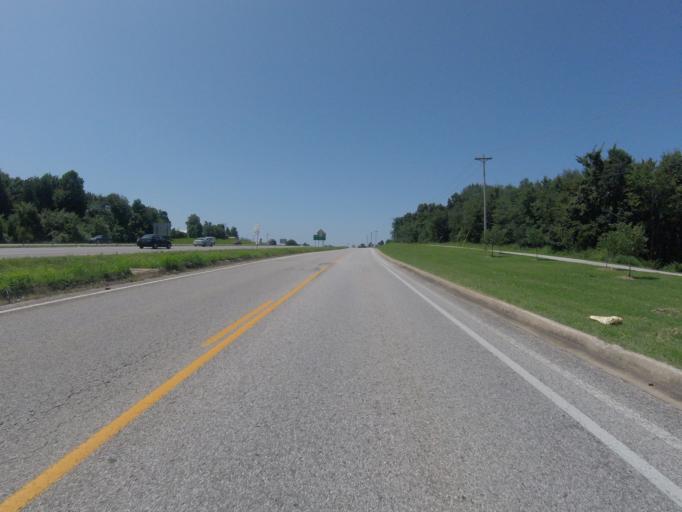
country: US
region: Arkansas
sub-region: Washington County
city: Johnson
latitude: 36.1002
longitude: -94.1852
